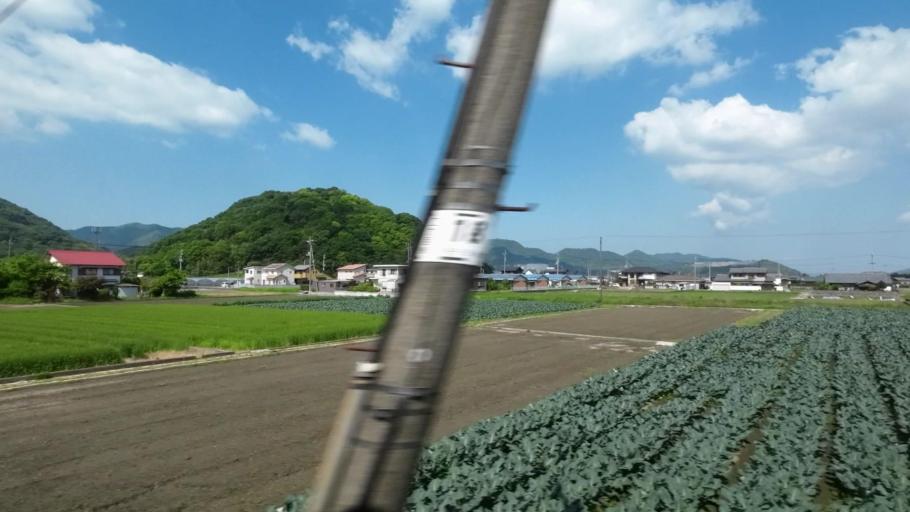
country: JP
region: Kagawa
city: Tadotsu
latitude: 34.1963
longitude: 133.7130
